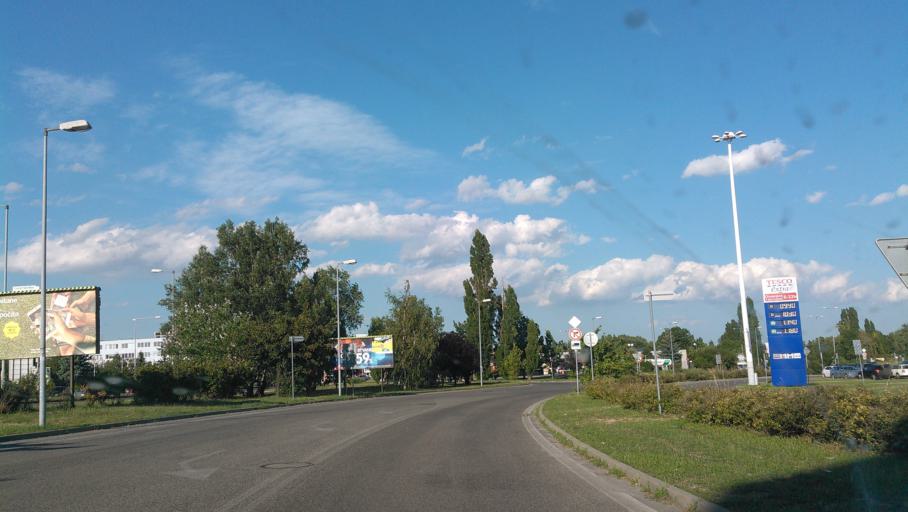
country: SK
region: Bratislavsky
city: Svaty Jur
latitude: 48.1878
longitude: 17.1777
